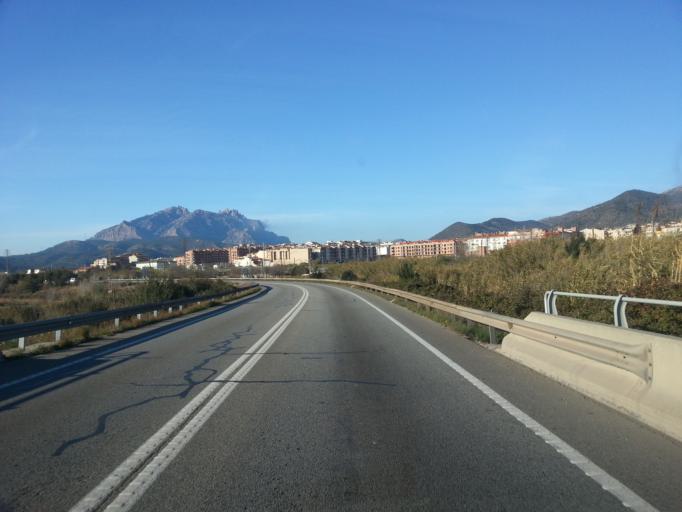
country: ES
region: Catalonia
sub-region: Provincia de Barcelona
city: Olesa de Montserrat
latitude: 41.5352
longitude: 1.8991
